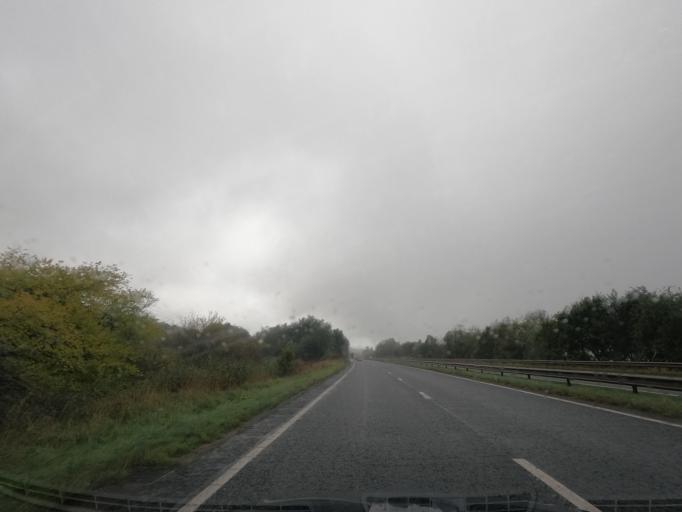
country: GB
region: England
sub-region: Redcar and Cleveland
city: South Bank
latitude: 54.5572
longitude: -1.1363
